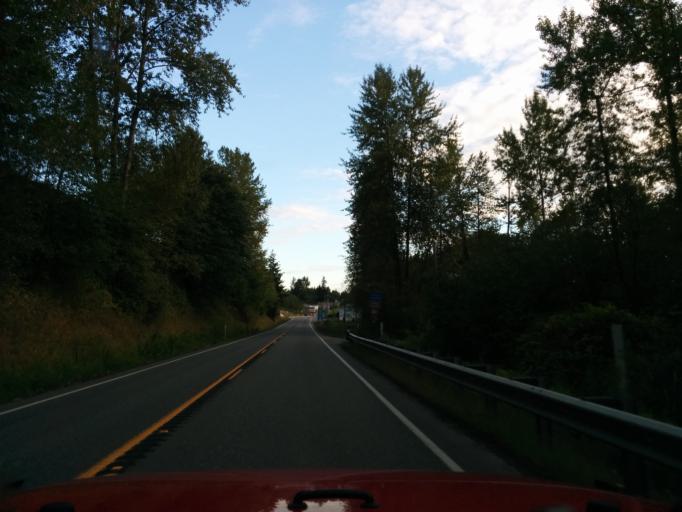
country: US
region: Washington
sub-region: King County
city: Duvall
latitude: 47.7473
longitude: -121.9859
